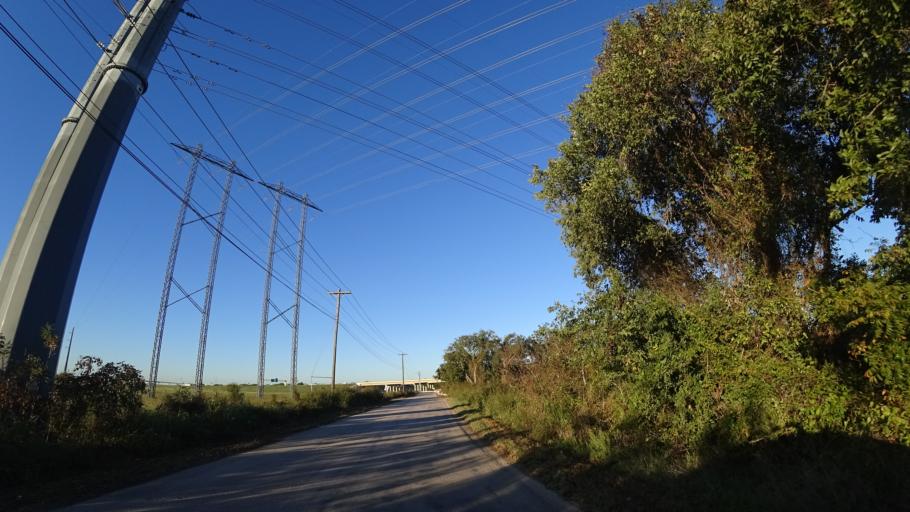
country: US
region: Texas
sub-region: Travis County
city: Hornsby Bend
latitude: 30.2104
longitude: -97.6194
